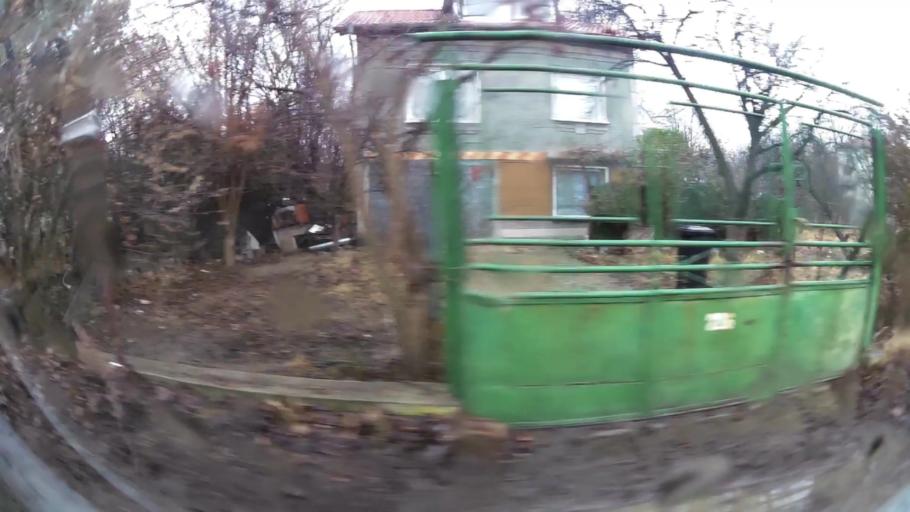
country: BG
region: Sofia-Capital
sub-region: Stolichna Obshtina
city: Sofia
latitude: 42.6552
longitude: 23.4291
